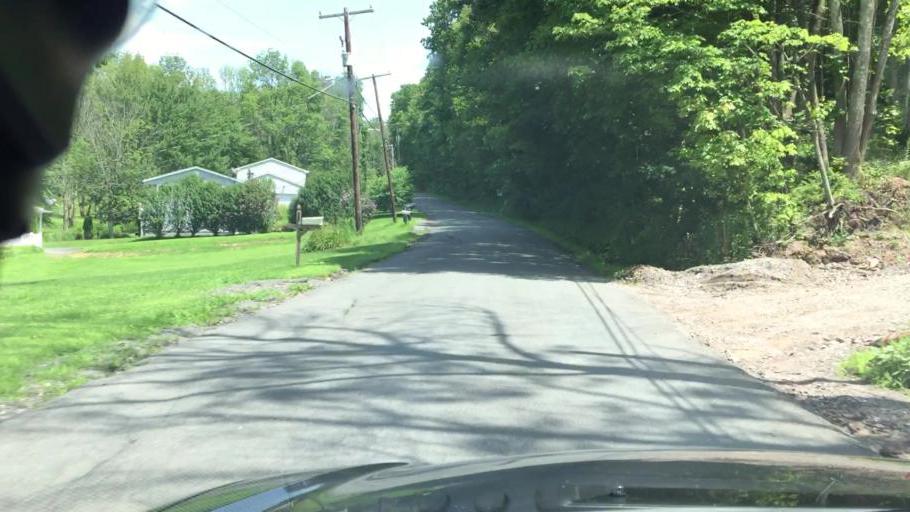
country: US
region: Pennsylvania
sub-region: Luzerne County
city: Oakdale
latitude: 41.0147
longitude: -75.9435
